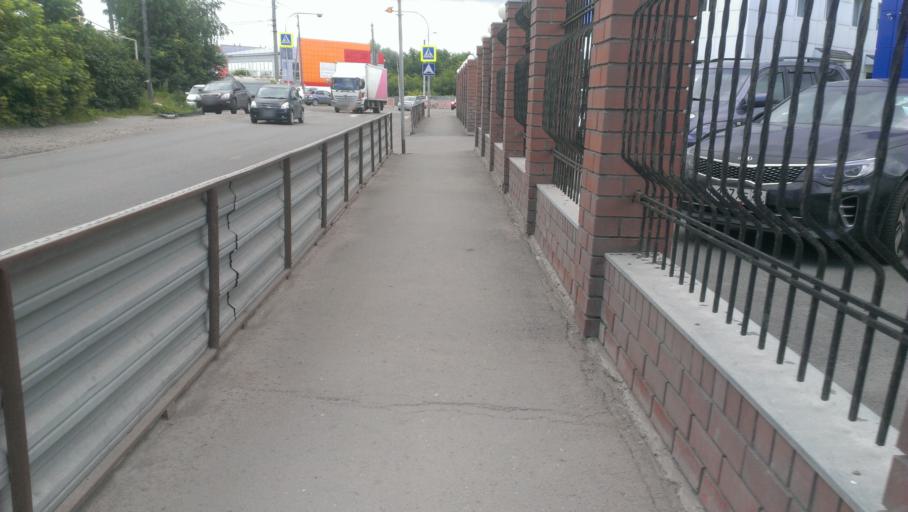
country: RU
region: Altai Krai
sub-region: Gorod Barnaulskiy
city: Barnaul
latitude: 53.3383
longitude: 83.7316
